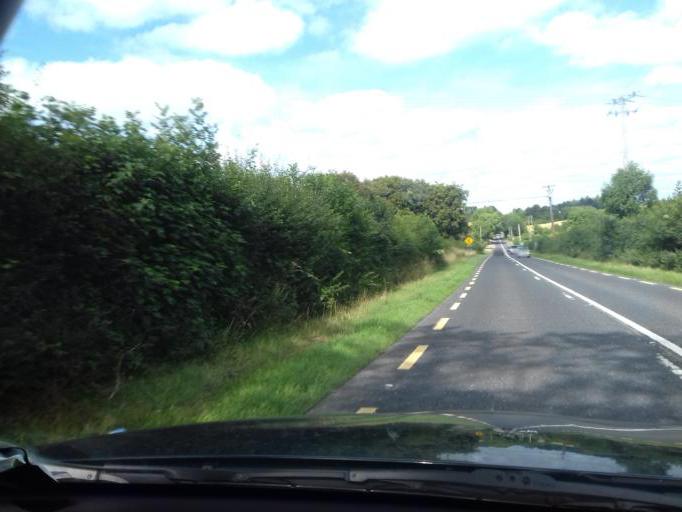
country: IE
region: Leinster
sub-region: Wicklow
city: Valleymount
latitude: 53.1115
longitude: -6.5966
